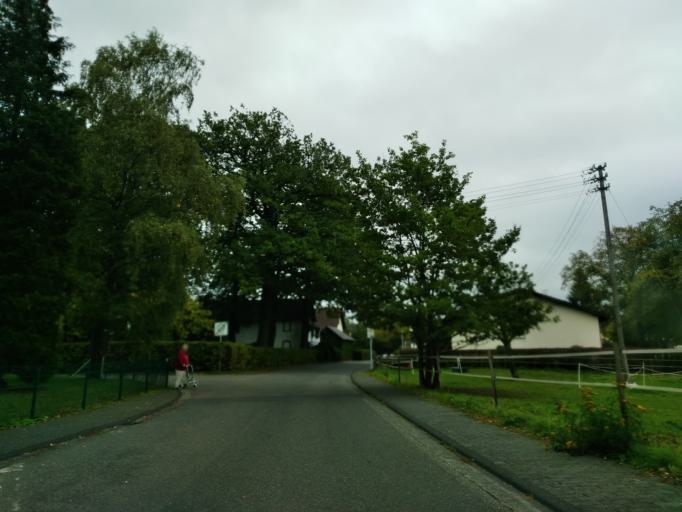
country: DE
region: Rheinland-Pfalz
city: Windhagen
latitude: 50.6377
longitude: 7.3243
